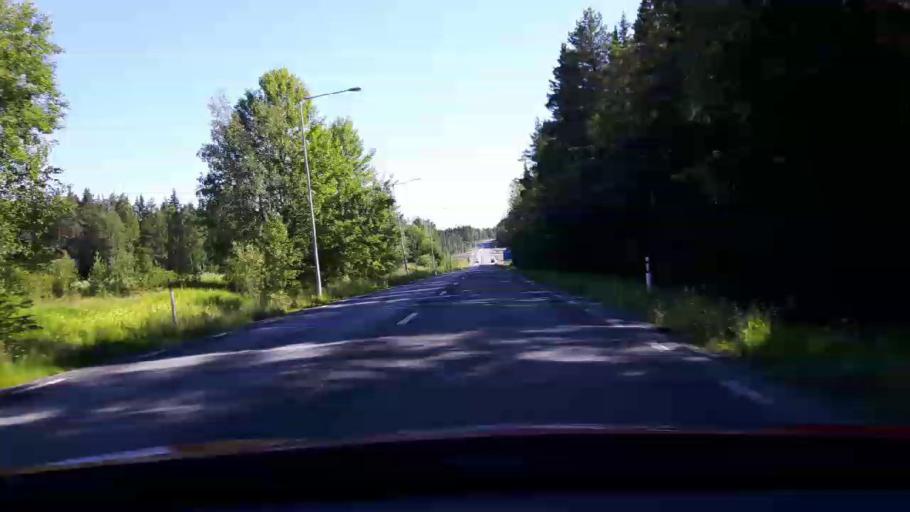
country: SE
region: Jaemtland
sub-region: OEstersunds Kommun
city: Ostersund
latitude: 63.1992
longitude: 14.6715
